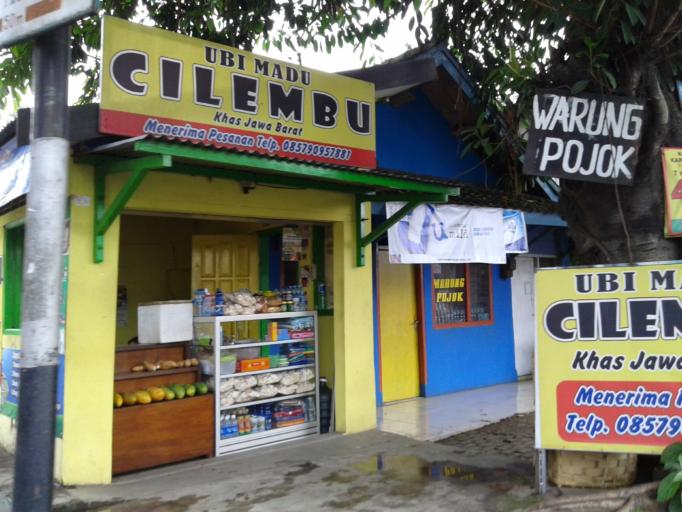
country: ID
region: East Java
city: Singosari
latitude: -7.9022
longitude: 112.6617
